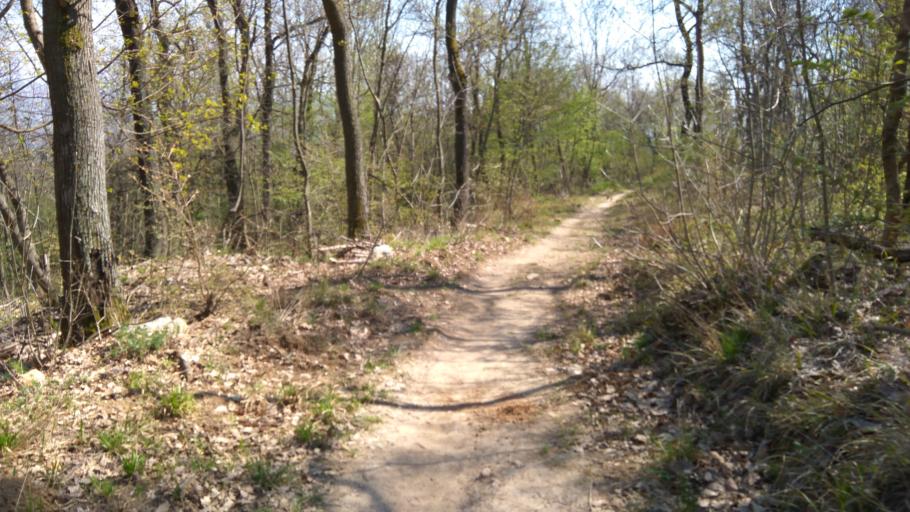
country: HU
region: Pest
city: Pilisborosjeno
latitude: 47.6231
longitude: 18.9903
